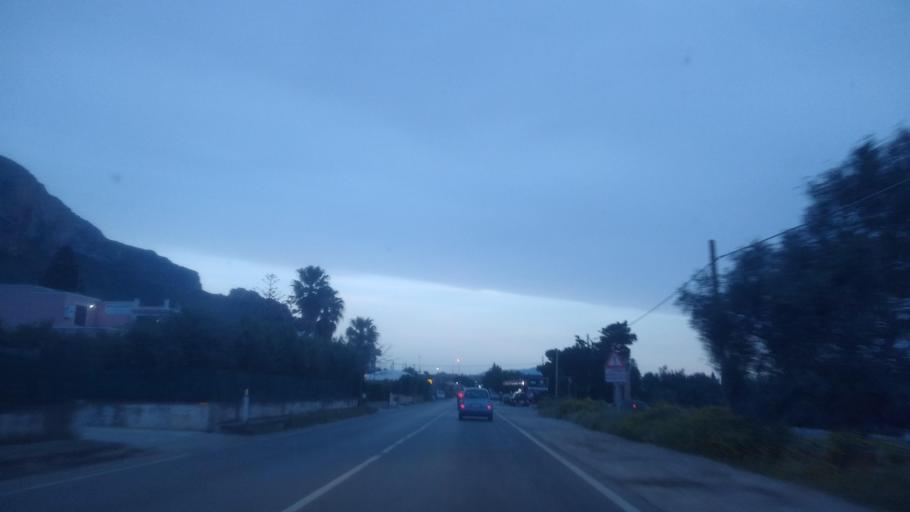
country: IT
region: Sicily
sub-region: Palermo
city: Terrasini
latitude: 38.1442
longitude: 13.0873
